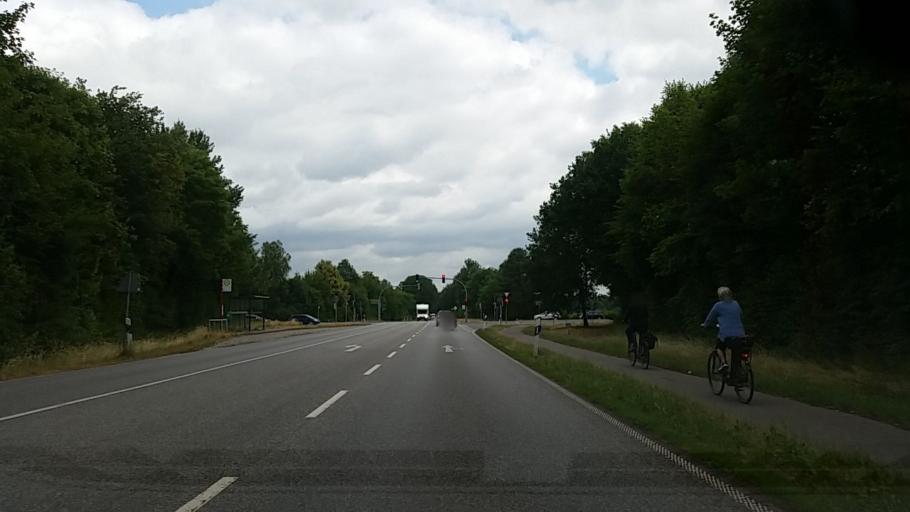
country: DE
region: Schleswig-Holstein
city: Tangstedt
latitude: 53.7271
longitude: 10.0986
